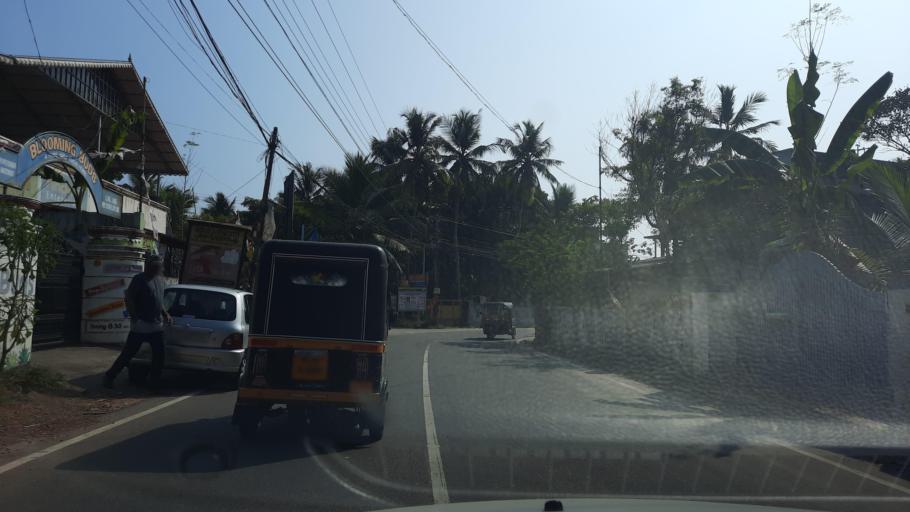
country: IN
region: Kerala
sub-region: Thiruvananthapuram
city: Thiruvananthapuram
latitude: 8.5666
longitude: 76.9226
